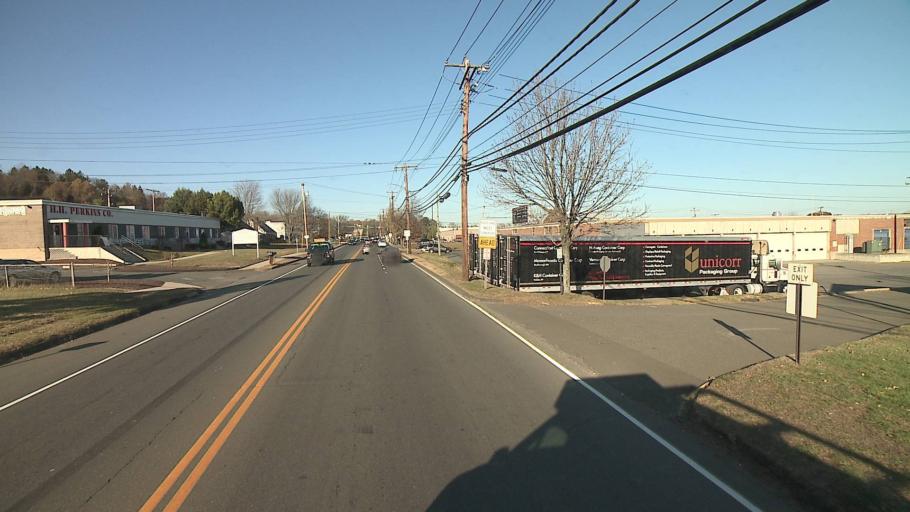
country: US
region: Connecticut
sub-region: New Haven County
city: Hamden
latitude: 41.3675
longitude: -72.8868
